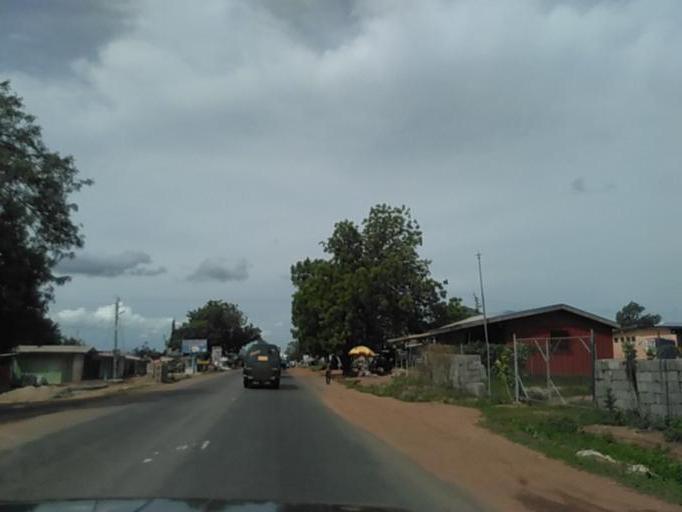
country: GH
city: Akropong
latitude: 6.2037
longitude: 0.0791
